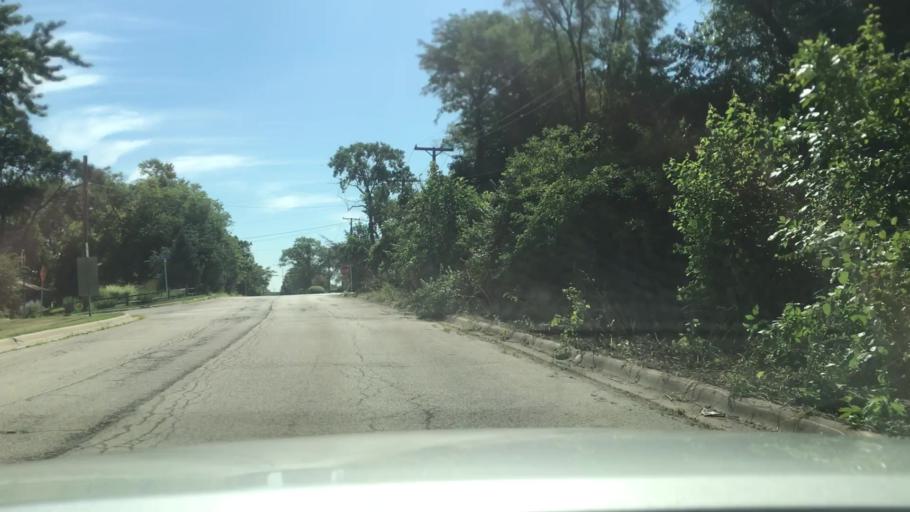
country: US
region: Illinois
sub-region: Cook County
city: Justice
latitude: 41.7402
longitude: -87.8328
